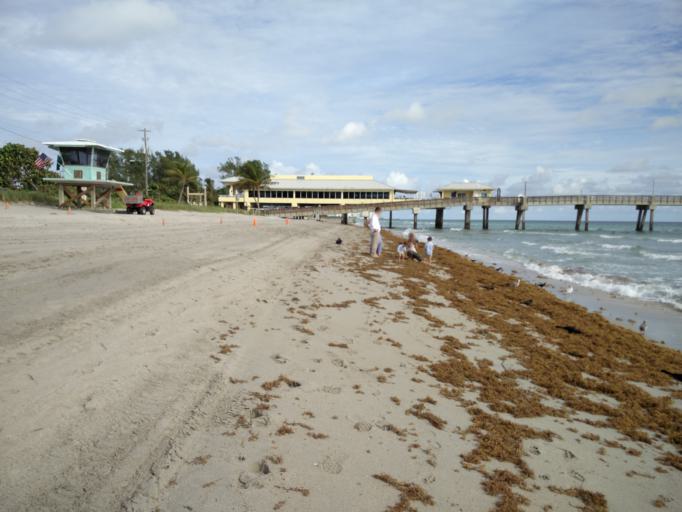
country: US
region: Florida
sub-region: Broward County
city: Dania Beach
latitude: 26.0572
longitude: -80.1115
